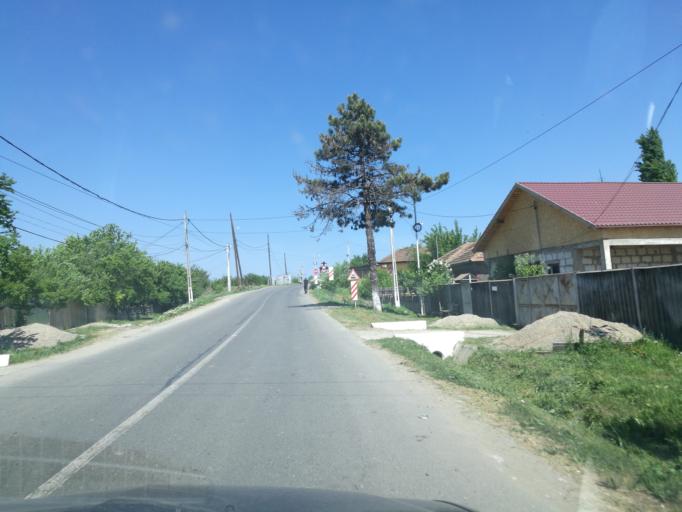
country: RO
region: Ialomita
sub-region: Comuna Adancata
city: Adancata
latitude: 44.7726
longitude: 26.4324
